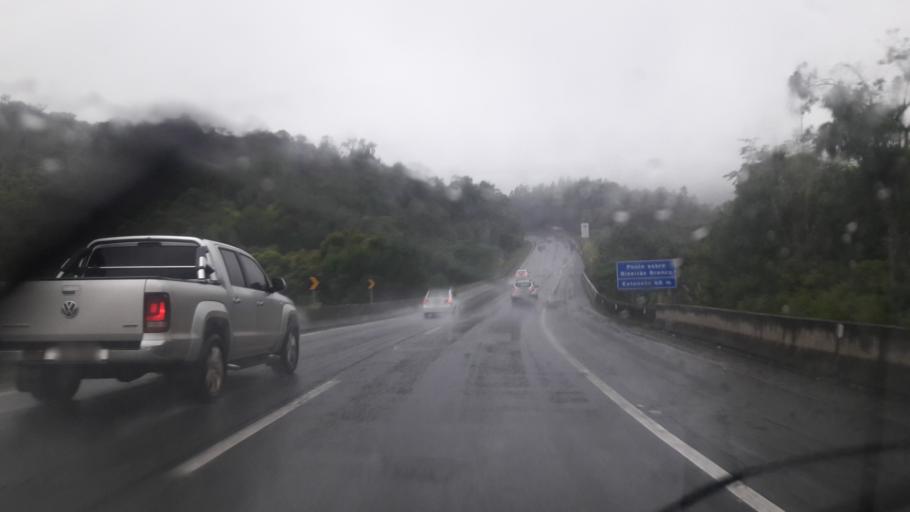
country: BR
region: Parana
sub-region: Antonina
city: Antonina
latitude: -25.1081
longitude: -48.7868
